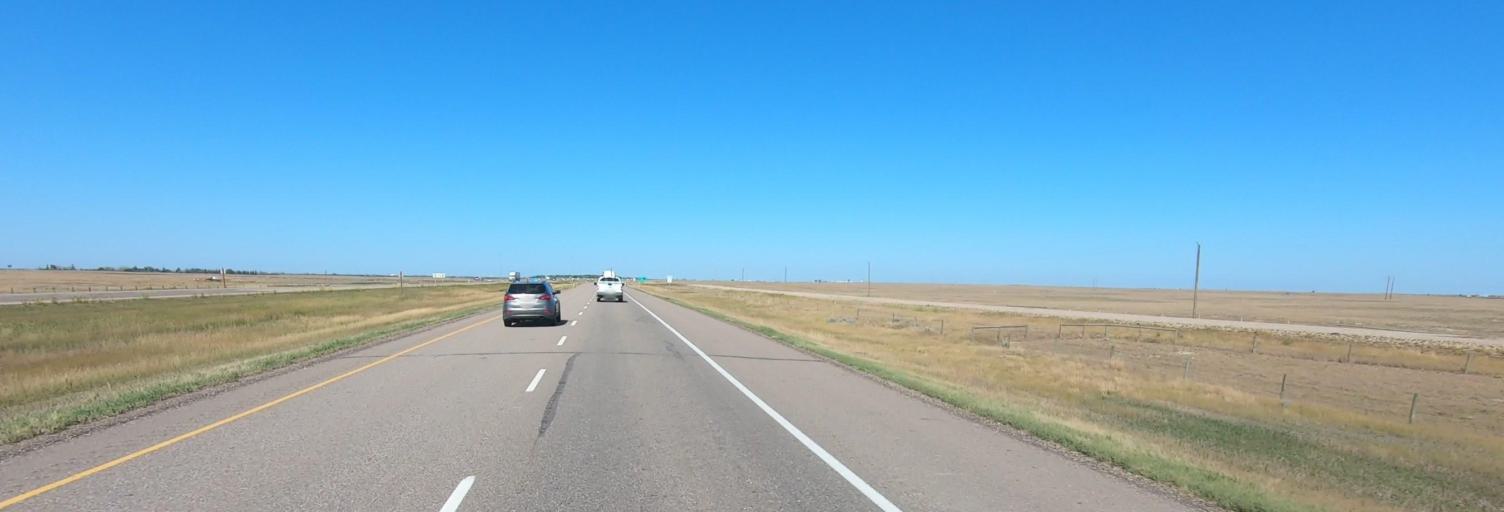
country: CA
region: Alberta
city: Brooks
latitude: 50.5206
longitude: -111.7533
